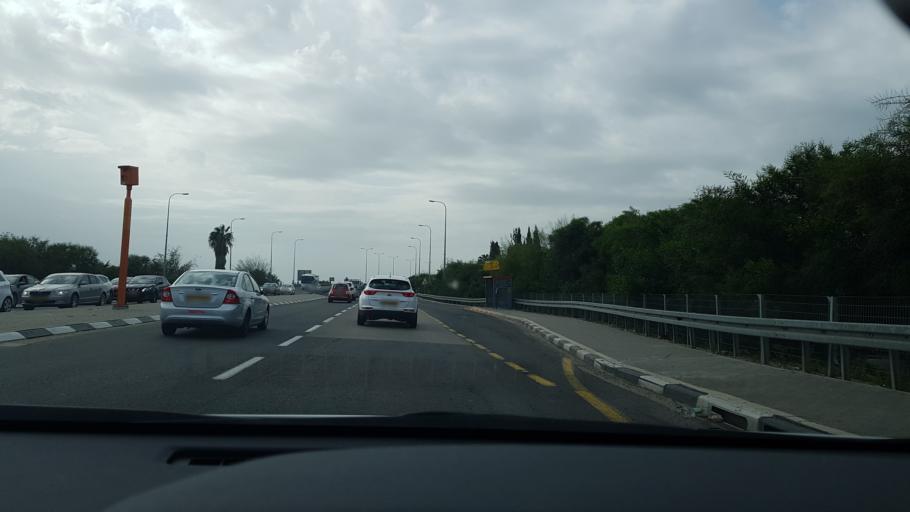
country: IL
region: Southern District
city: Ashqelon
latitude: 31.6659
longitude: 34.6065
